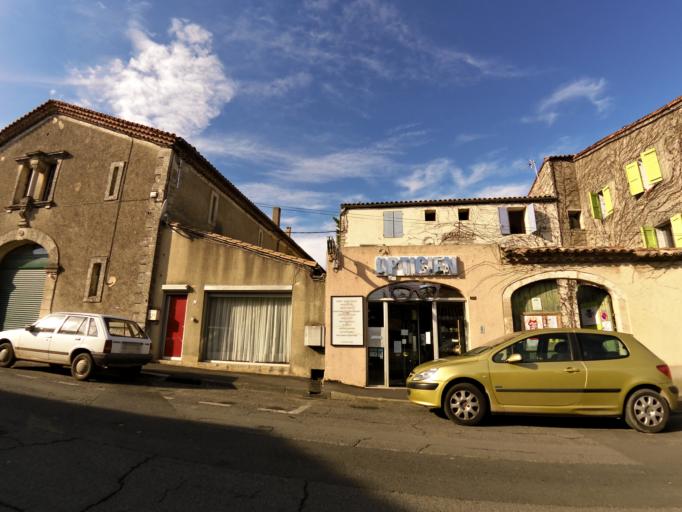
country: FR
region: Languedoc-Roussillon
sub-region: Departement de l'Herault
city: Saint-Martin-de-Londres
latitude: 43.7895
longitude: 3.7325
